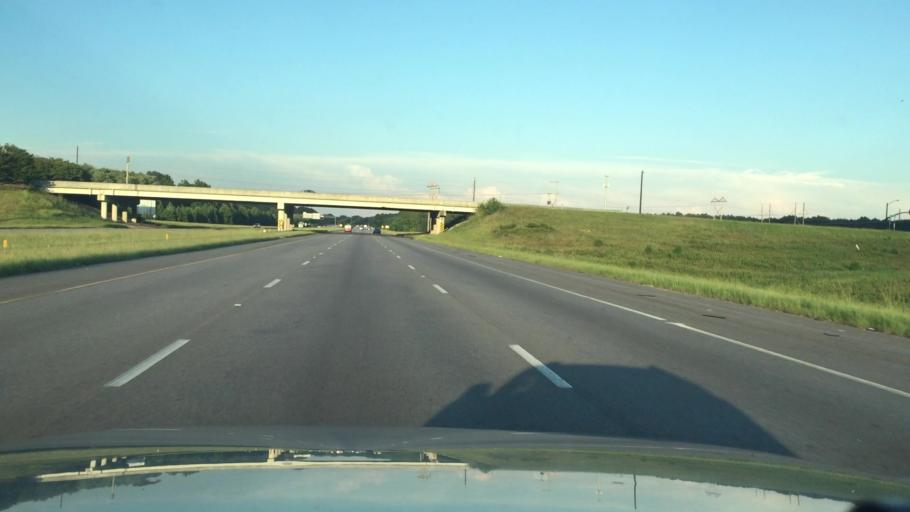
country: US
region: South Carolina
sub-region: Lexington County
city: Cayce
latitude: 33.9291
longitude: -81.0443
